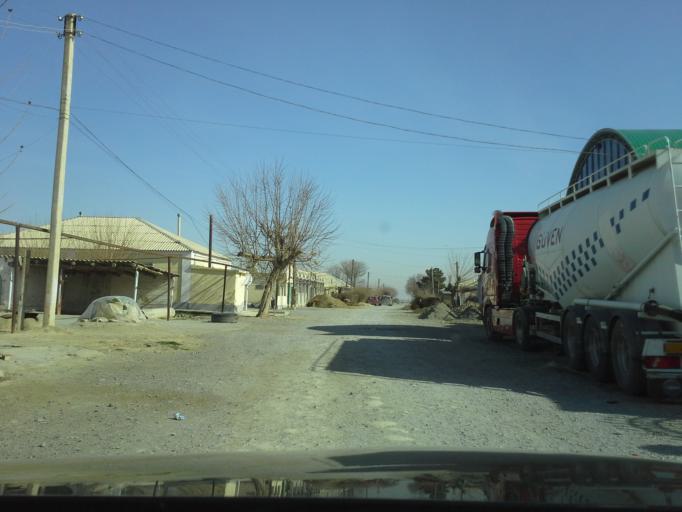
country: TM
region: Ahal
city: Arcabil
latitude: 38.1055
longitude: 57.9794
